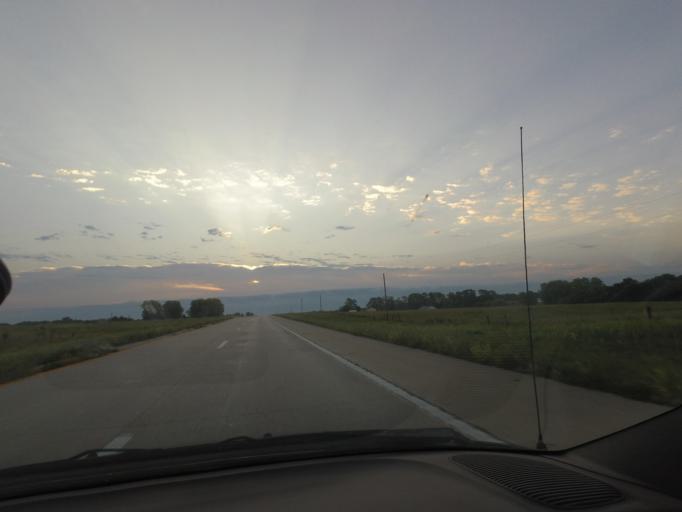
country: US
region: Missouri
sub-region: Macon County
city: Macon
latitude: 39.7503
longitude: -92.3626
